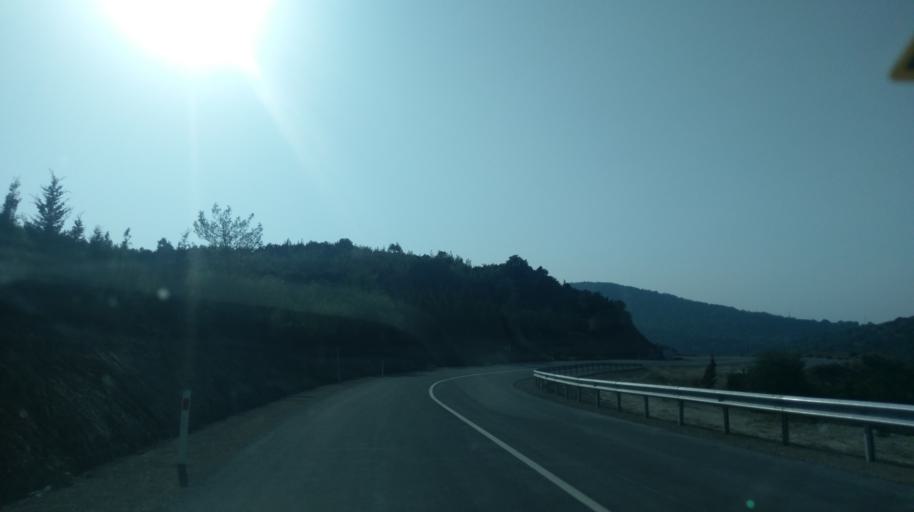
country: CY
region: Ammochostos
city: Leonarisso
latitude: 35.5362
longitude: 34.2560
